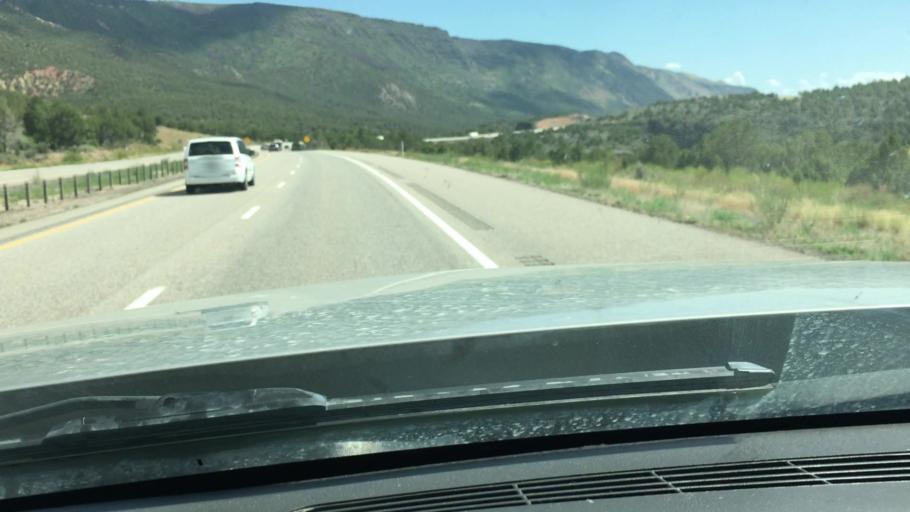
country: US
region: Utah
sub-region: Washington County
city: Toquerville
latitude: 37.4202
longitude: -113.2358
